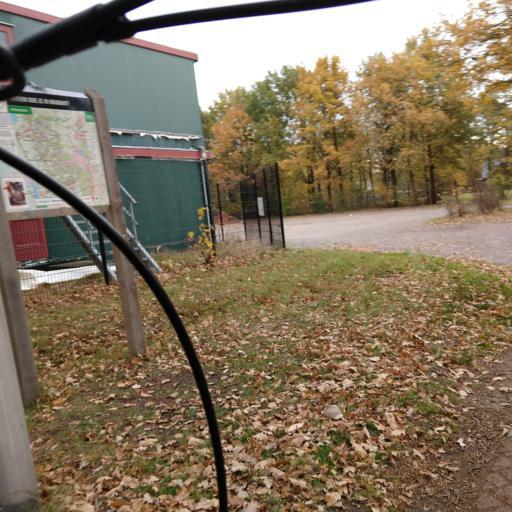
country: BE
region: Flanders
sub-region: Provincie Antwerpen
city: Stabroek
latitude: 51.3696
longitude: 4.3990
